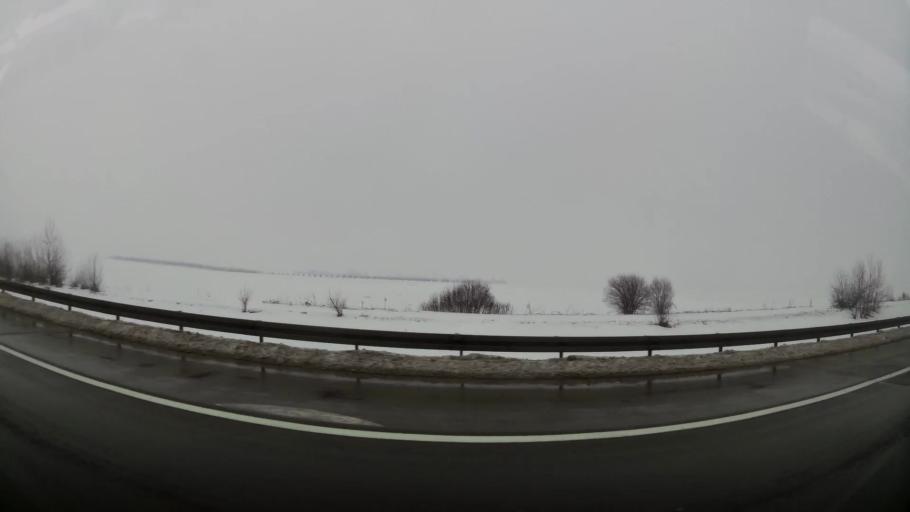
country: RS
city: Dobanovci
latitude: 44.8272
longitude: 20.2518
